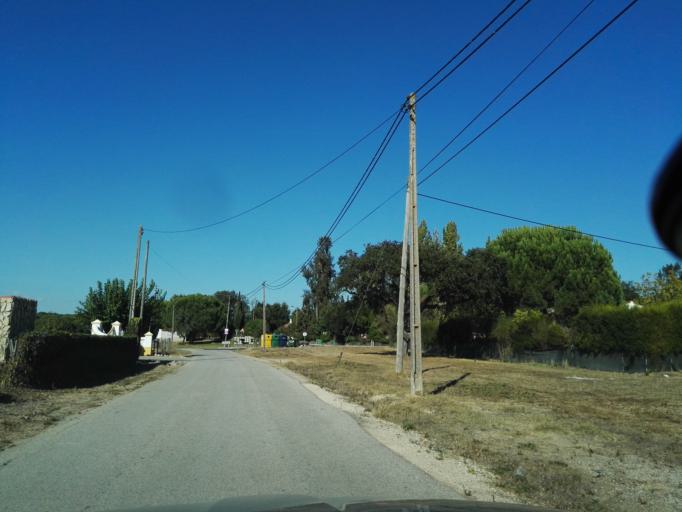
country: PT
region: Santarem
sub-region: Benavente
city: Poceirao
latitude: 38.8632
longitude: -8.7373
